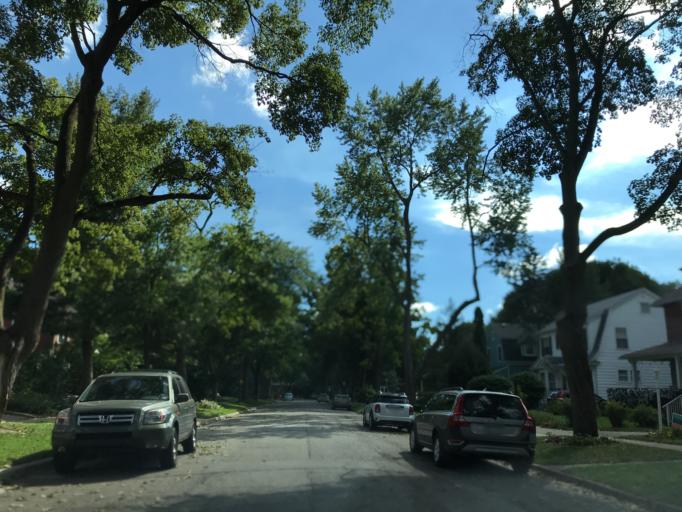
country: US
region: Michigan
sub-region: Washtenaw County
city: Ann Arbor
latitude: 42.2659
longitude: -83.7314
